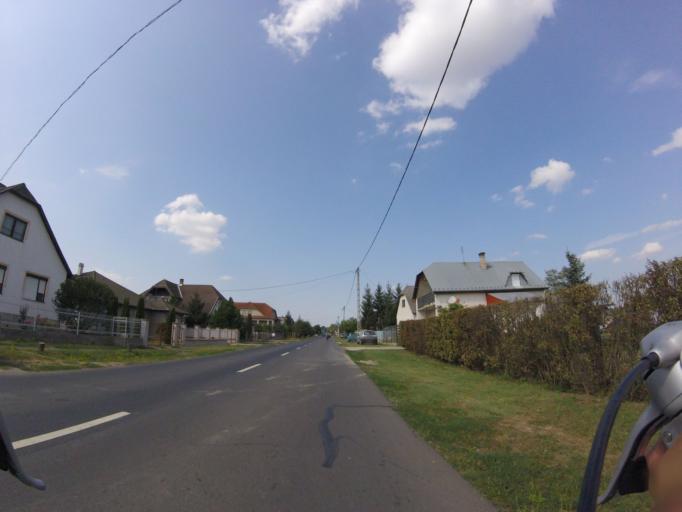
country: HU
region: Szabolcs-Szatmar-Bereg
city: Anarcs
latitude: 48.1818
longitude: 22.1043
